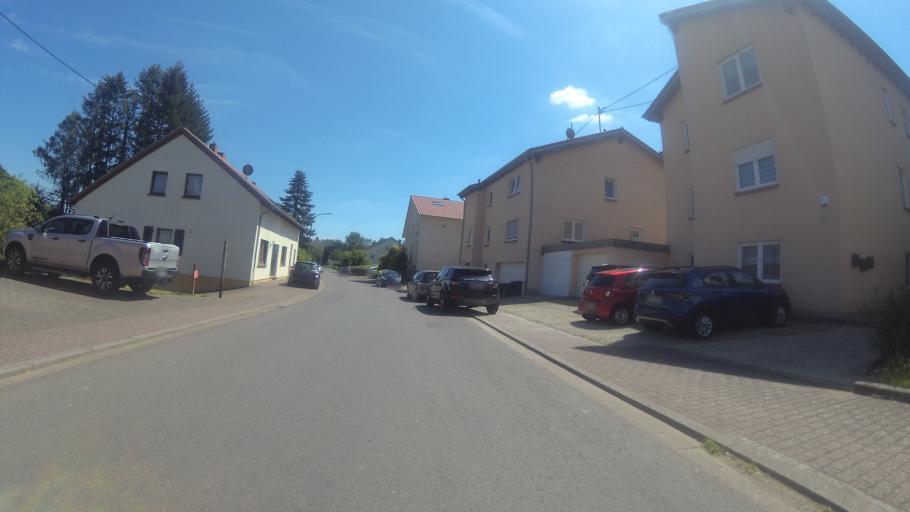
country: DE
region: Saarland
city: Heusweiler
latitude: 49.3435
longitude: 6.8946
